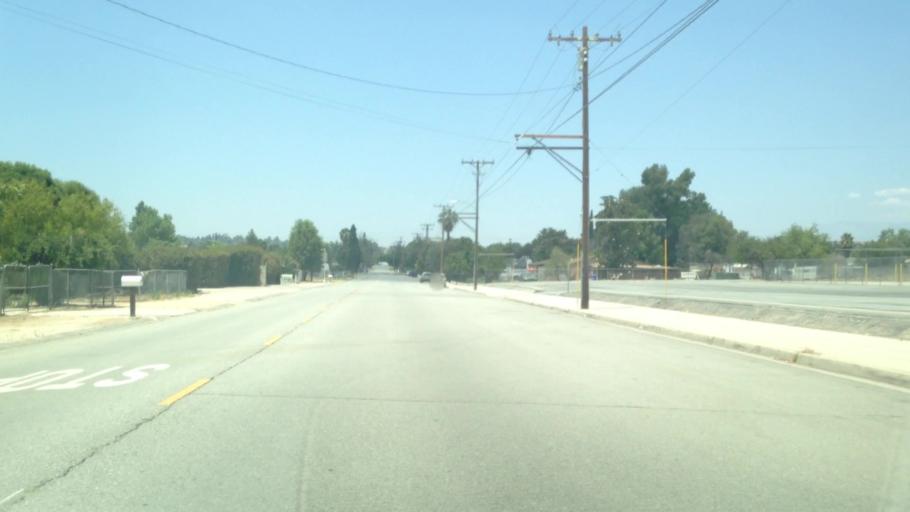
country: US
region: California
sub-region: Riverside County
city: Calimesa
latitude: 34.0266
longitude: -117.0877
